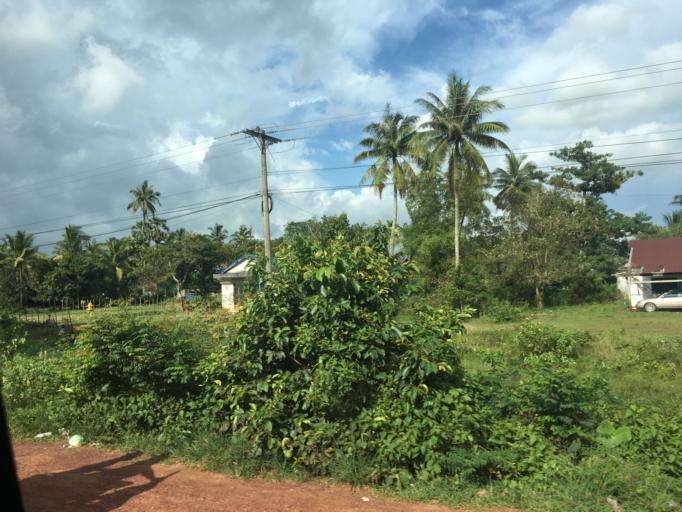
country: KH
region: Preah Sihanouk
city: Sihanoukville
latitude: 10.6417
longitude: 103.7864
